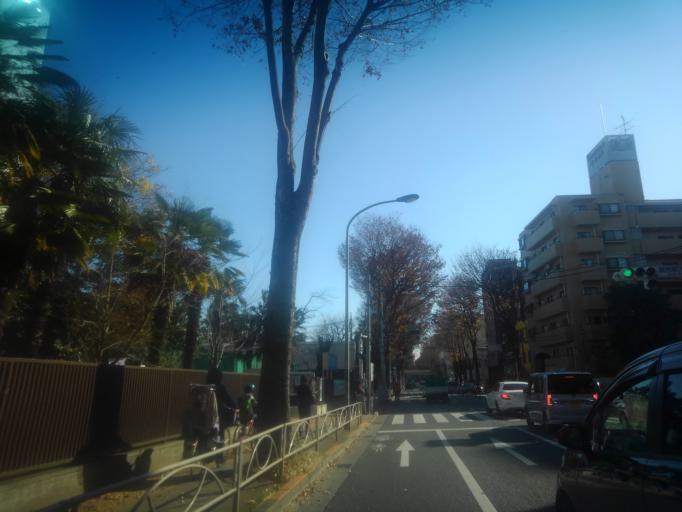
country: JP
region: Tokyo
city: Chofugaoka
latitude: 35.6553
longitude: 139.5443
